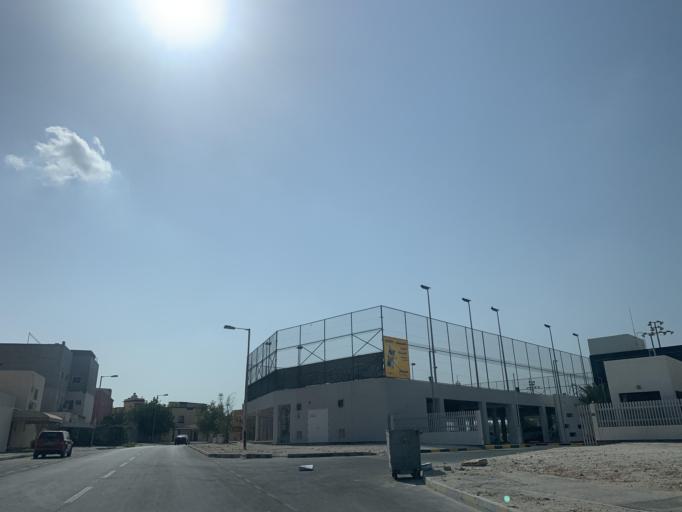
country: BH
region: Central Governorate
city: Madinat Hamad
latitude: 26.1359
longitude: 50.5064
